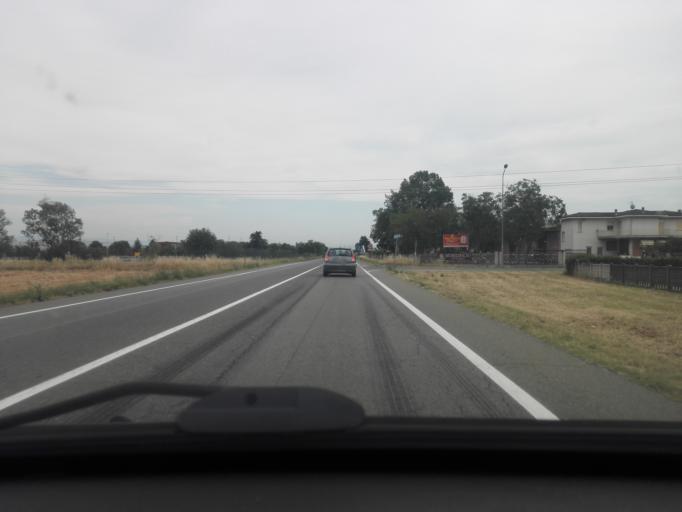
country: IT
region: Piedmont
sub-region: Provincia di Alessandria
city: Mandrogne
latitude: 44.8312
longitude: 8.7406
